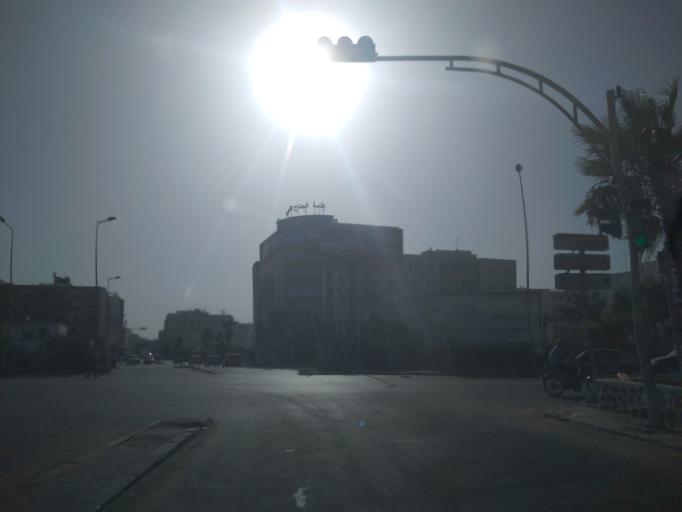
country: TN
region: Safaqis
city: Sfax
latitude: 34.7464
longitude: 10.7661
